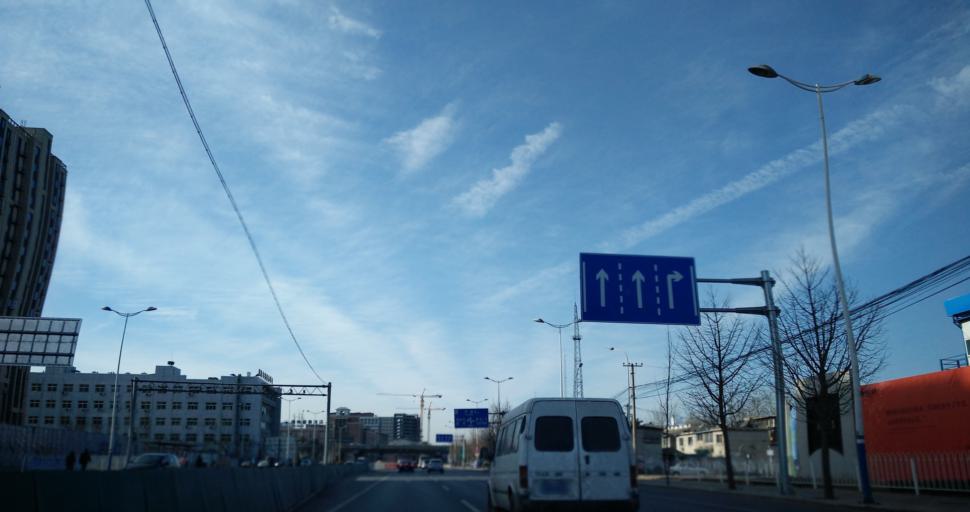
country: CN
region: Beijing
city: Xingfeng
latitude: 39.7414
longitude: 116.3422
